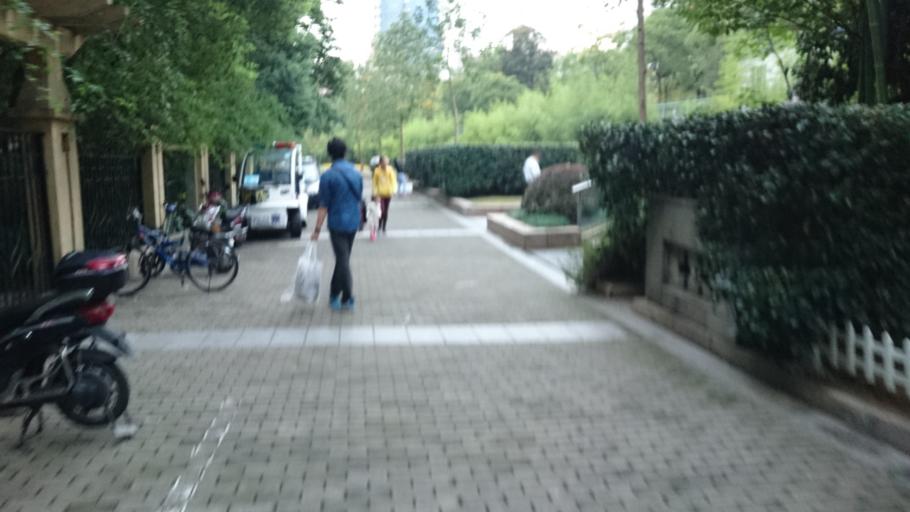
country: CN
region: Shanghai Shi
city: Shanghai
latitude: 31.2346
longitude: 121.4702
